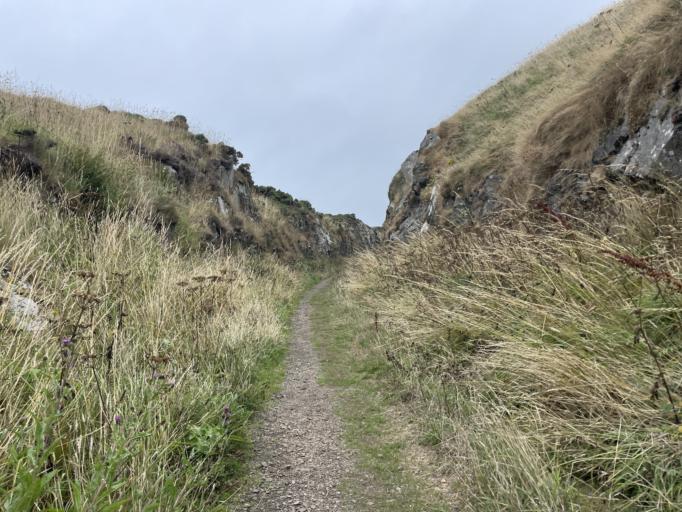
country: GB
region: Scotland
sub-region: Dumfries and Galloway
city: Stranraer
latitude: 54.8370
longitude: -5.1119
